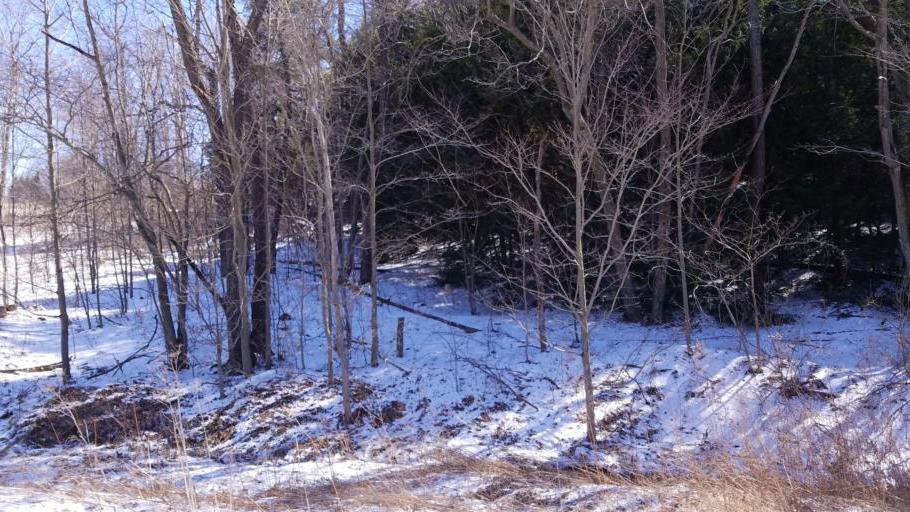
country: US
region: New York
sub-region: Allegany County
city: Andover
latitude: 42.0156
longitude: -77.7726
